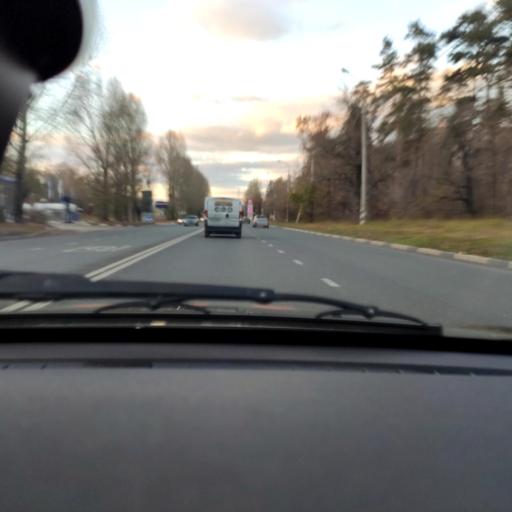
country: RU
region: Samara
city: Zhigulevsk
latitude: 53.5071
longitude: 49.4651
